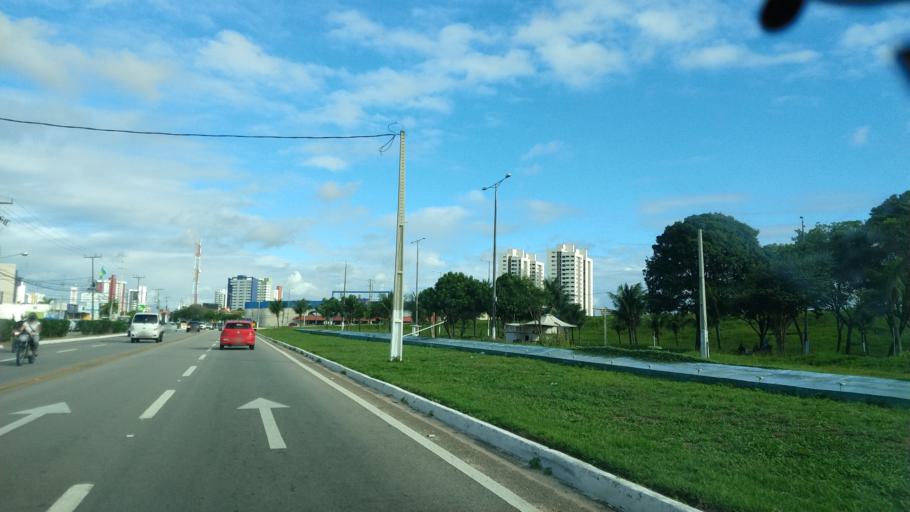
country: BR
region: Rio Grande do Norte
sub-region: Natal
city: Natal
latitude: -5.8474
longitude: -35.2078
